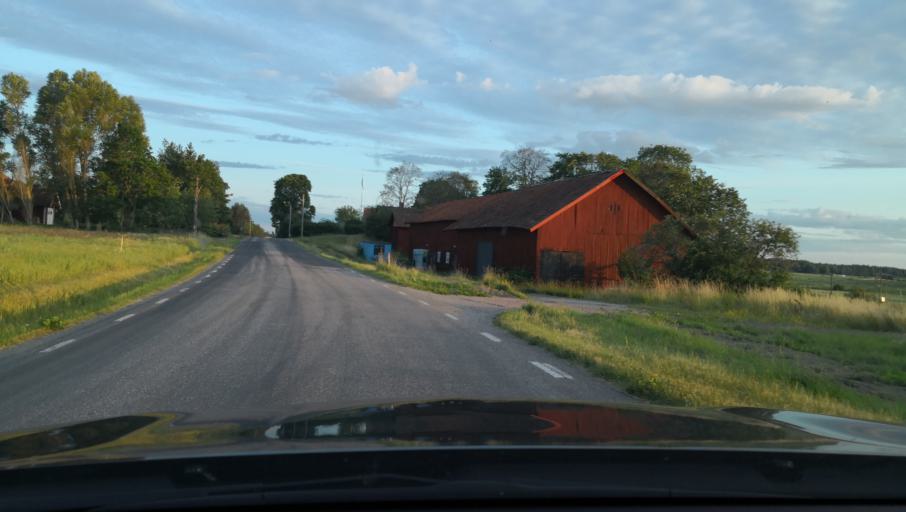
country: SE
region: Uppsala
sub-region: Uppsala Kommun
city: Vattholma
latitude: 60.0217
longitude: 17.7216
